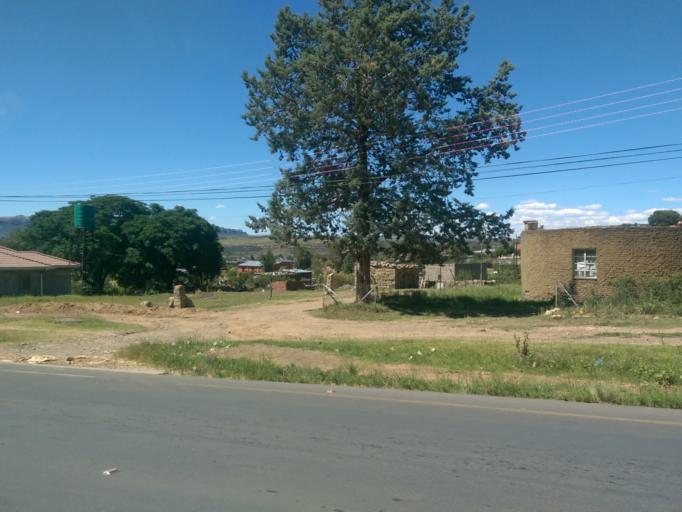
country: LS
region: Maseru
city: Maseru
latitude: -29.4163
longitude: 27.5598
